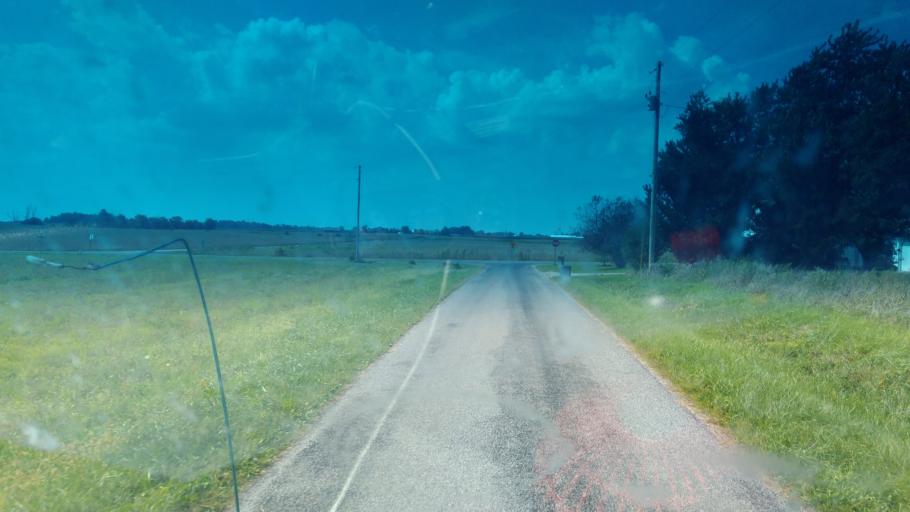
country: US
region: Ohio
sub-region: Hardin County
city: Ada
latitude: 40.6819
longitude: -83.8791
